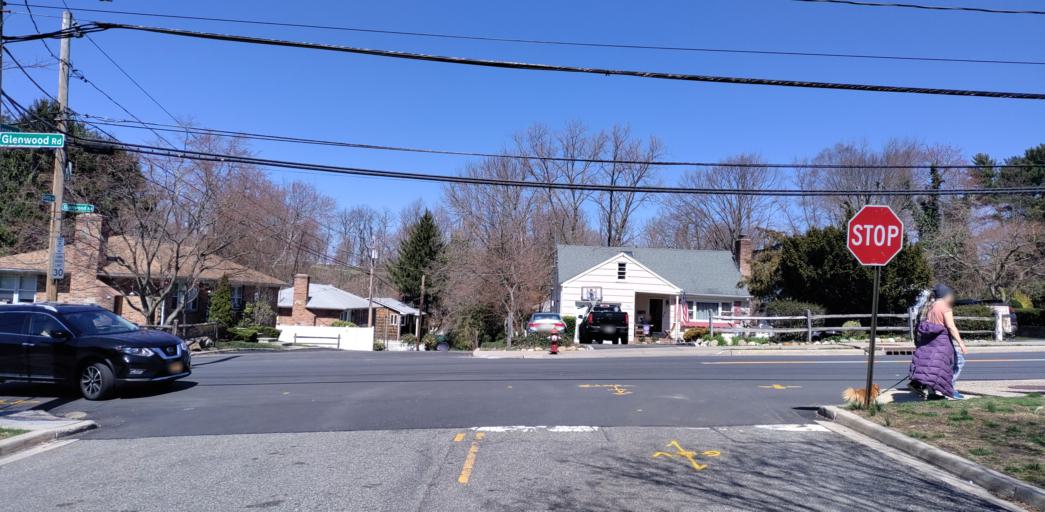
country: US
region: New York
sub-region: Nassau County
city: Glenwood Landing
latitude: 40.8302
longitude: -73.6411
